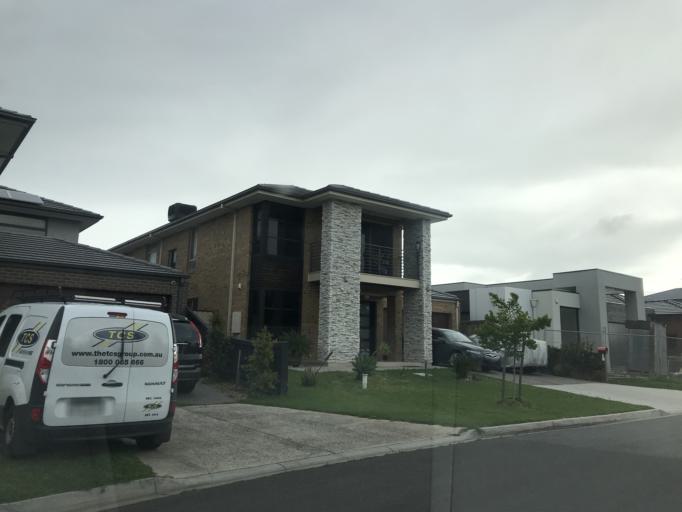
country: AU
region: Victoria
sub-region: Brimbank
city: Sunshine West
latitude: -37.7960
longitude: 144.8015
